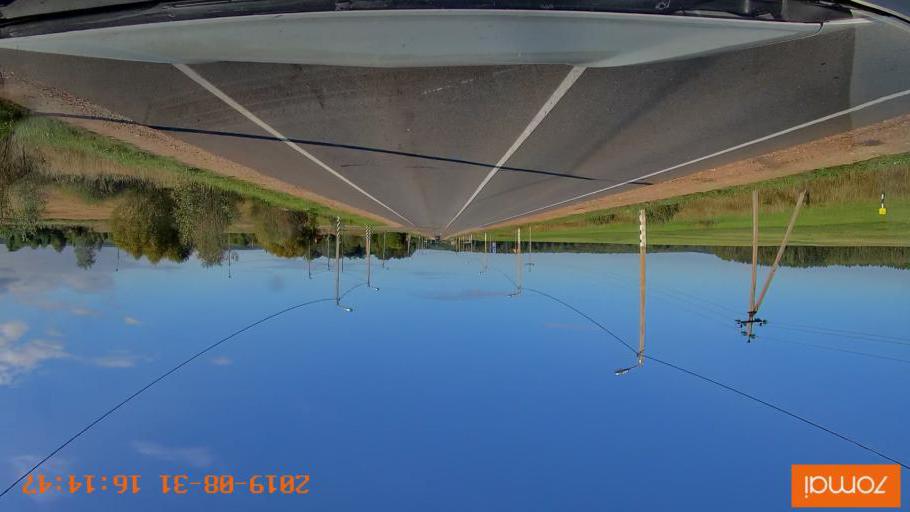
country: RU
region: Kaluga
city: Nikola-Lenivets
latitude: 54.5643
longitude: 35.4750
